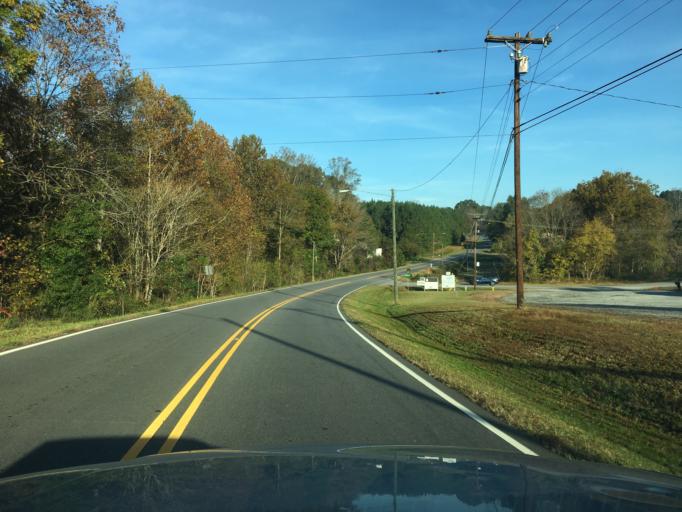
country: US
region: North Carolina
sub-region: Catawba County
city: Newton
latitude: 35.6852
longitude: -81.2528
